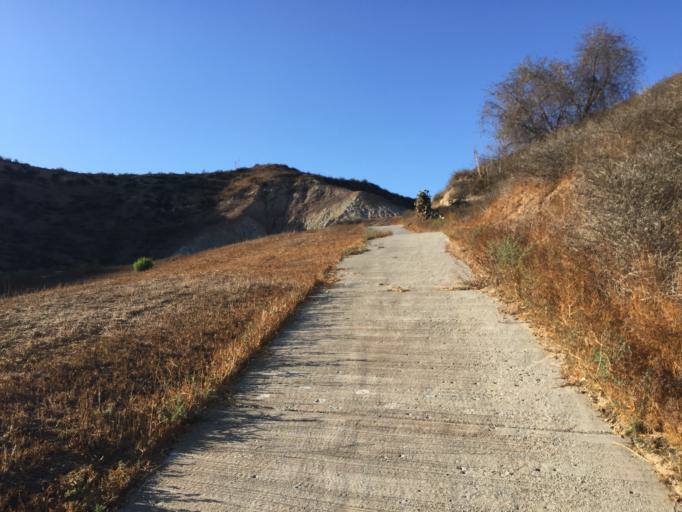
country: US
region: California
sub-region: Ventura County
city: Simi Valley
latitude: 34.3004
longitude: -118.7504
